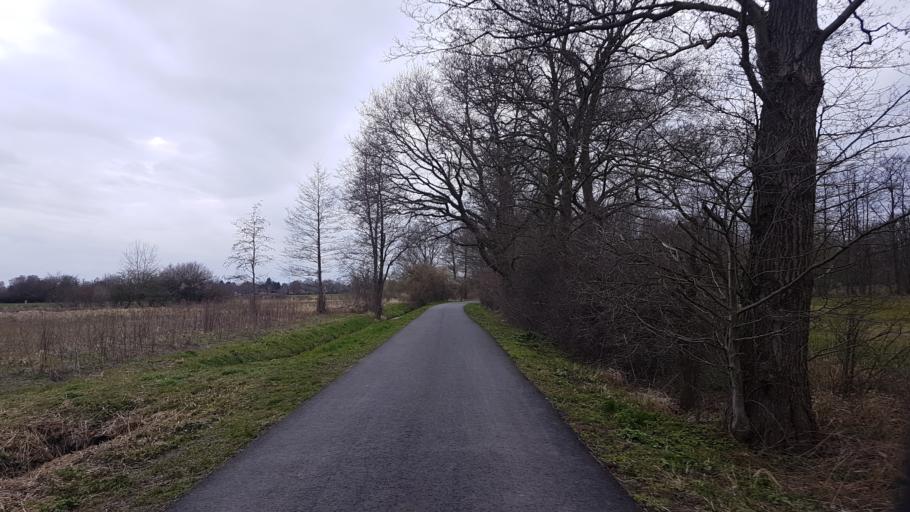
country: DE
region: Lower Saxony
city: Isernhagen Farster Bauerschaft
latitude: 52.4400
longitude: 9.8116
